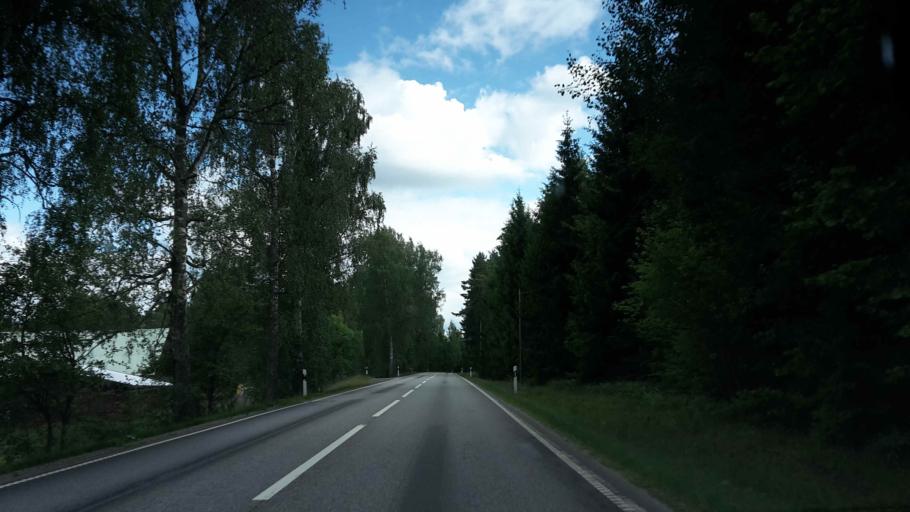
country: SE
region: OErebro
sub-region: Hallsbergs Kommun
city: Palsboda
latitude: 58.8168
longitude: 15.4136
